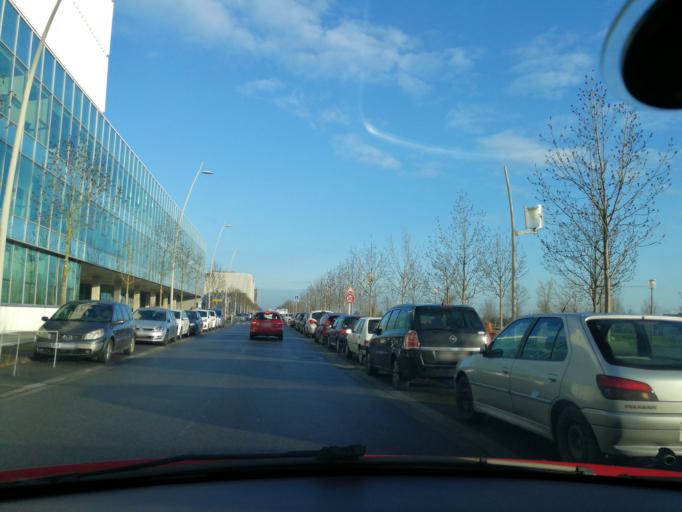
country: FR
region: Midi-Pyrenees
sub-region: Departement de la Haute-Garonne
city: Beauzelle
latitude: 43.6564
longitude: 1.3671
